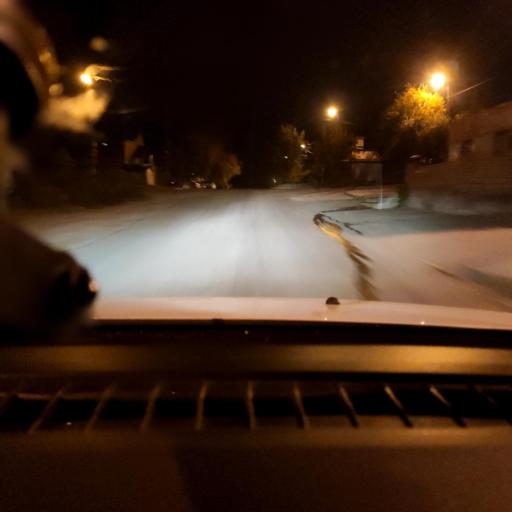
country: RU
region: Samara
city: Samara
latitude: 53.1836
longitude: 50.2056
